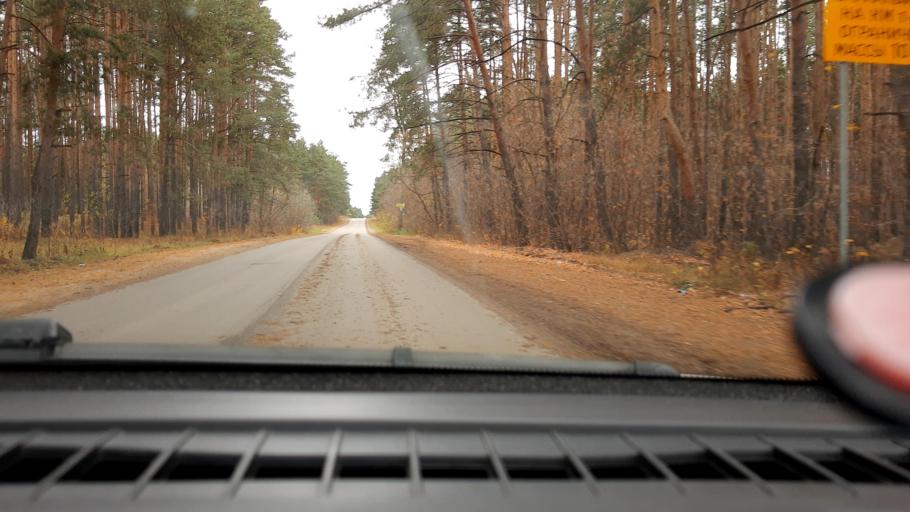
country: RU
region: Nizjnij Novgorod
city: Lukino
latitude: 56.3914
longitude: 43.7395
